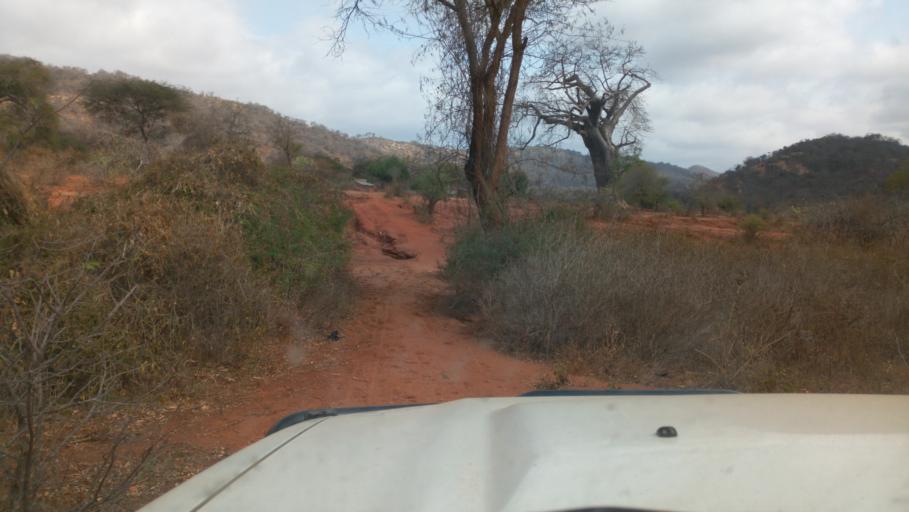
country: KE
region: Kitui
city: Kitui
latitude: -1.8393
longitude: 38.2966
